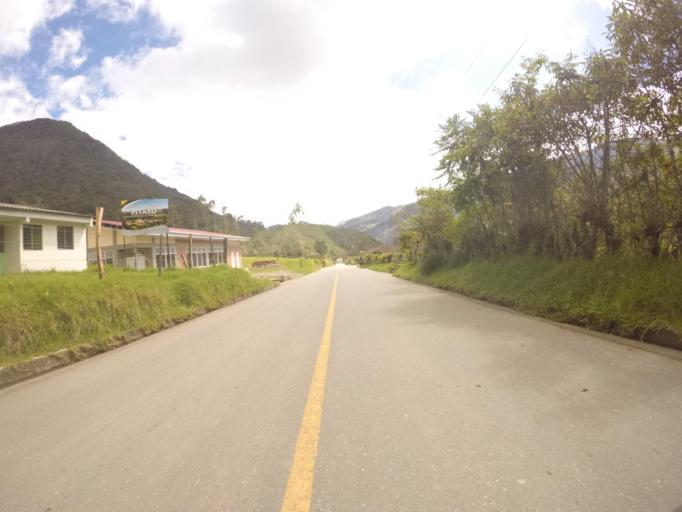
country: CO
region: Cauca
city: Jambalo
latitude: 2.7164
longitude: -76.3251
